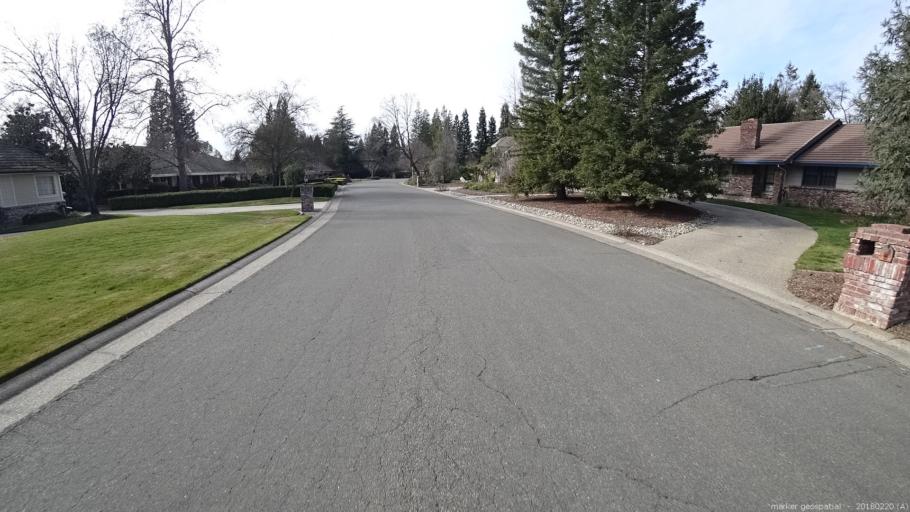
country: US
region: California
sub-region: Sacramento County
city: Orangevale
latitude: 38.7161
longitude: -121.2356
